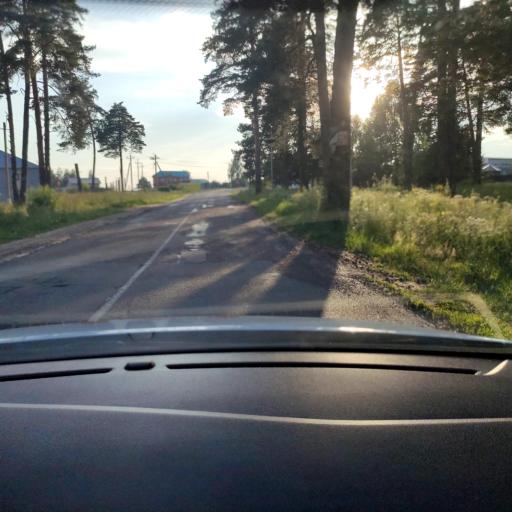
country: RU
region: Tatarstan
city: Vysokaya Gora
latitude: 55.9673
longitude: 49.2981
